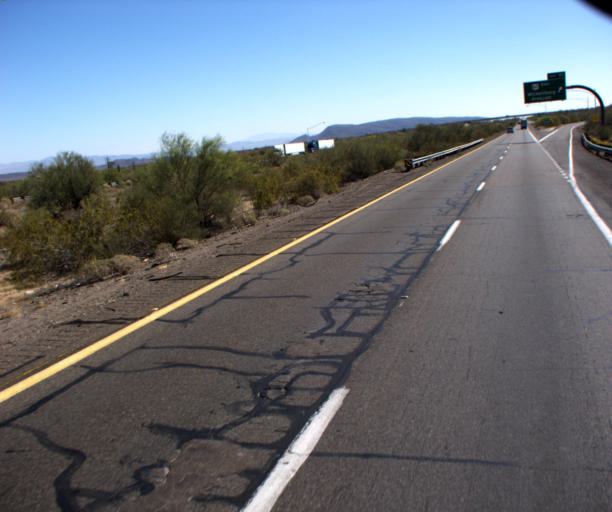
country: US
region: Arizona
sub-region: La Paz County
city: Quartzsite
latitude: 33.6627
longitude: -114.0211
